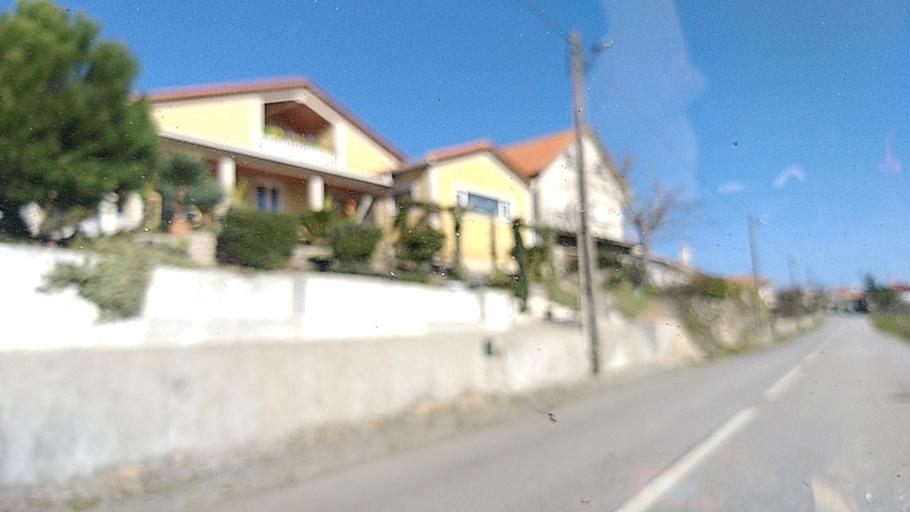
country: PT
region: Guarda
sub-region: Celorico da Beira
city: Celorico da Beira
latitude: 40.6531
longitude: -7.4649
